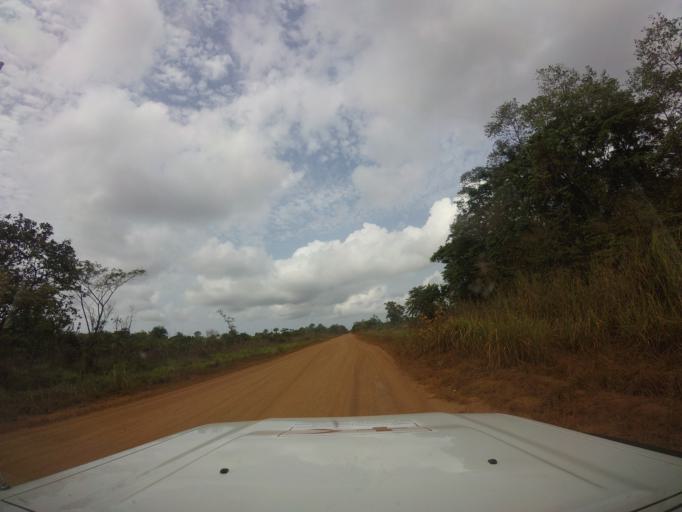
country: LR
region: Grand Cape Mount
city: Robertsport
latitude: 6.6852
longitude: -11.1243
